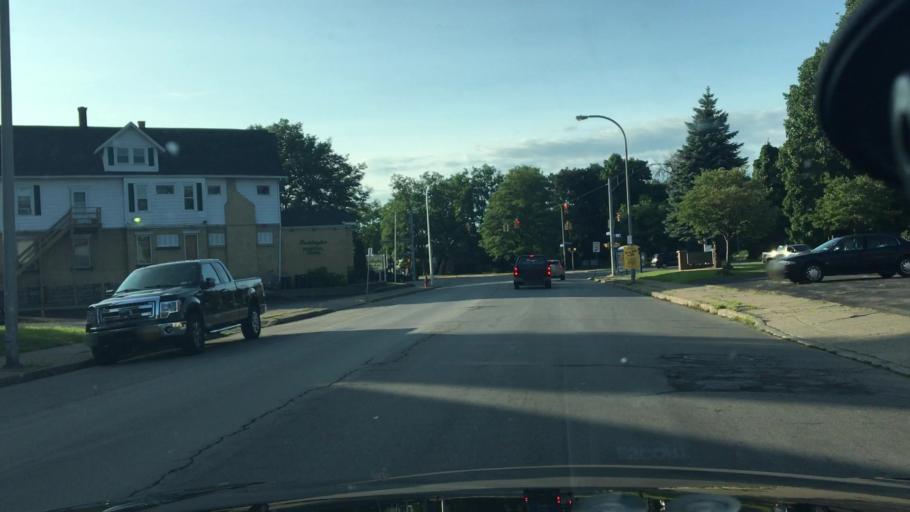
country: US
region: New York
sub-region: Erie County
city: West Seneca
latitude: 42.8457
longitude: -78.8099
